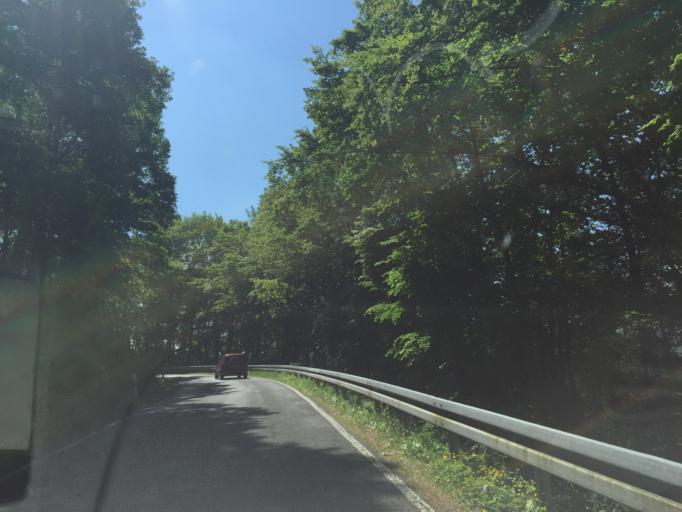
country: DE
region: Bavaria
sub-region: Regierungsbezirk Unterfranken
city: Weilbach
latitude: 49.6457
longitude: 9.2614
